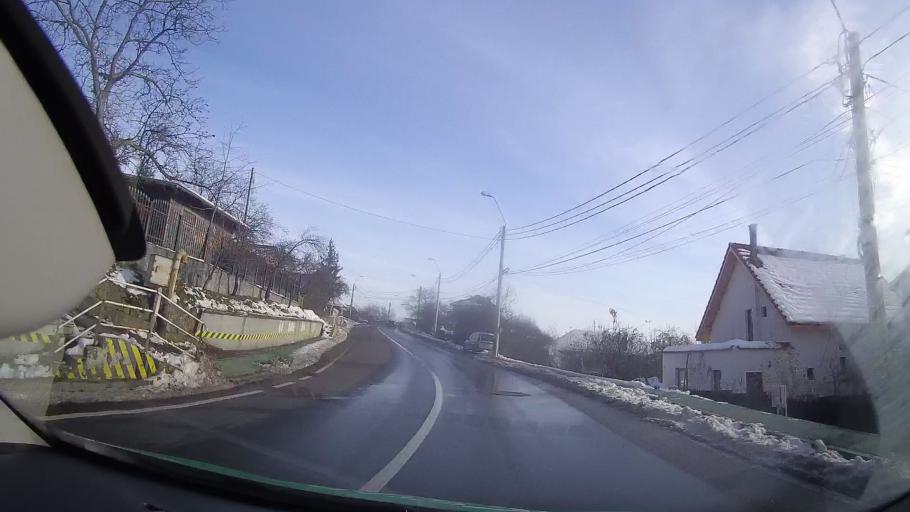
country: RO
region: Neamt
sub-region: Comuna Garcina
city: Garcina
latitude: 46.9723
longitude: 26.3673
